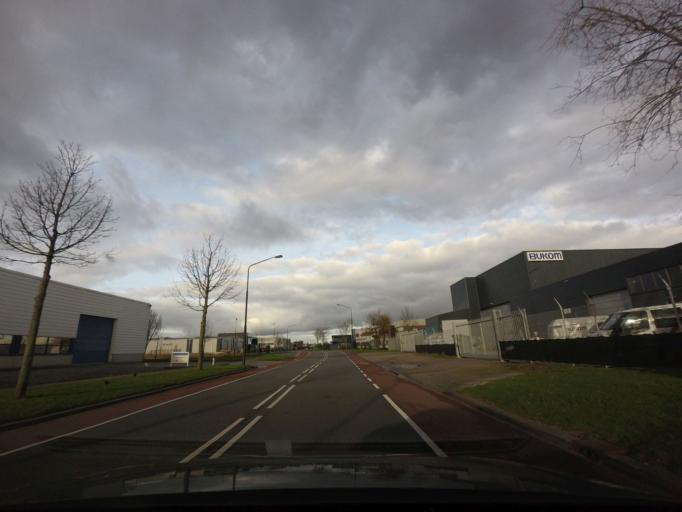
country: NL
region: North Holland
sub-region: Gemeente Heerhugowaard
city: Heerhugowaard
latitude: 52.6865
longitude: 4.8343
